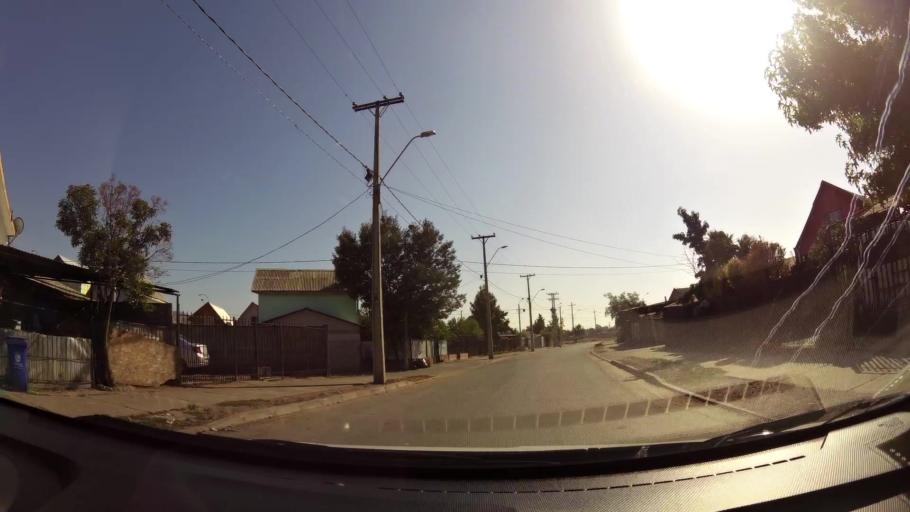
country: CL
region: Maule
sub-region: Provincia de Talca
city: Talca
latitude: -35.3988
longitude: -71.6545
